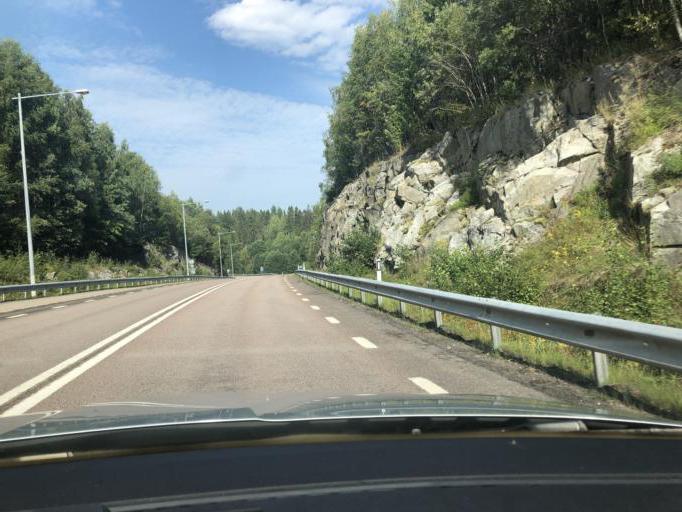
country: SE
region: Vaesternorrland
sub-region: Kramfors Kommun
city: Kramfors
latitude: 62.8000
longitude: 17.8722
